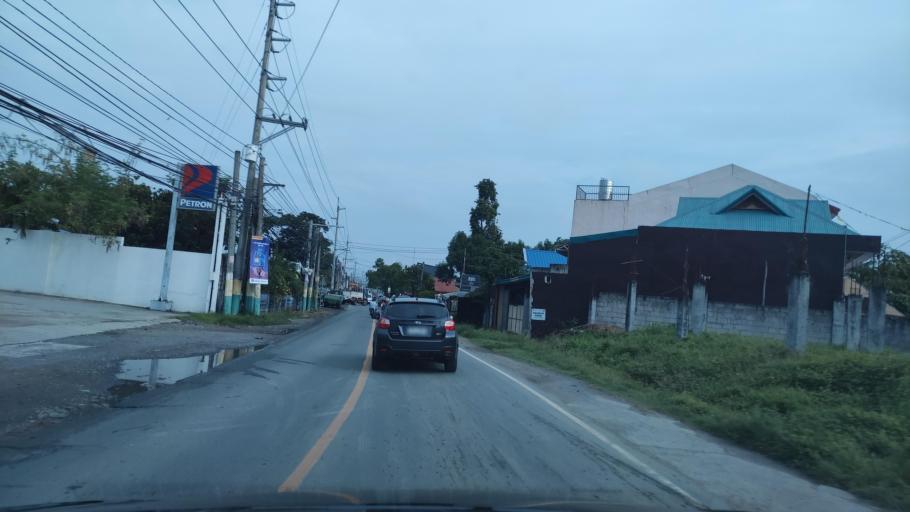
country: PH
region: Central Luzon
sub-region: Province of Pampanga
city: Arayat
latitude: 15.1436
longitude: 120.7711
